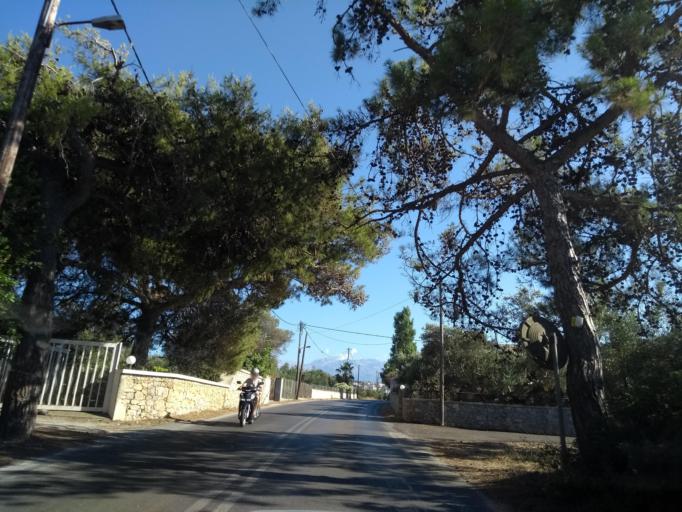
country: GR
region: Crete
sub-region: Nomos Chanias
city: Pithari
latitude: 35.5440
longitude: 24.0824
